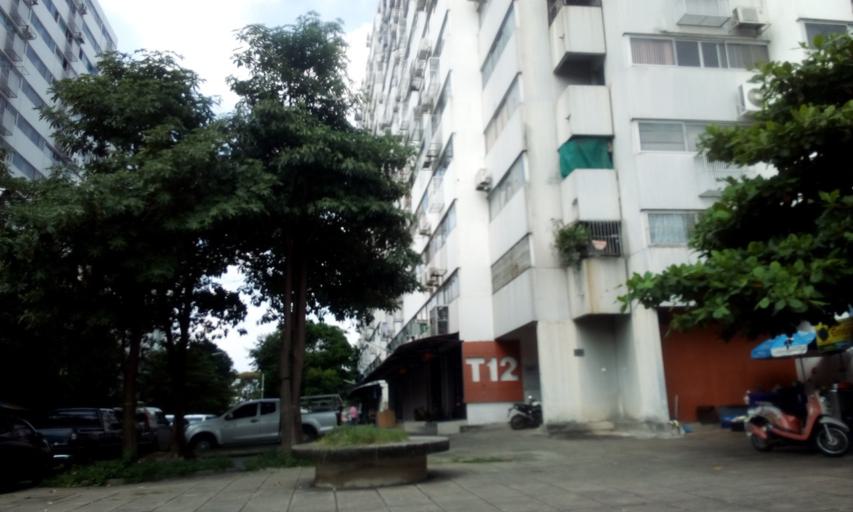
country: TH
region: Bangkok
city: Don Mueang
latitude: 13.9179
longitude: 100.5545
